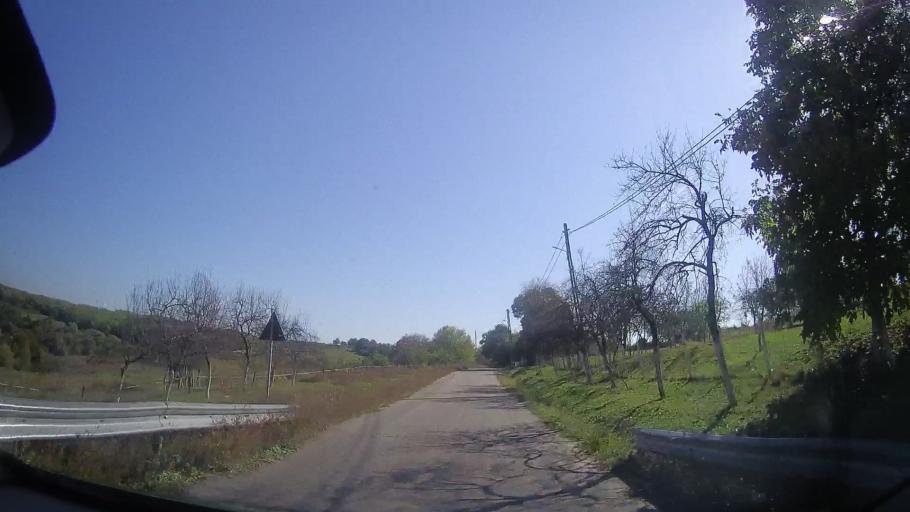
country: RO
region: Timis
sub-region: Comuna Ohaba Lunga
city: Ohaba Lunga
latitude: 45.9118
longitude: 21.9424
